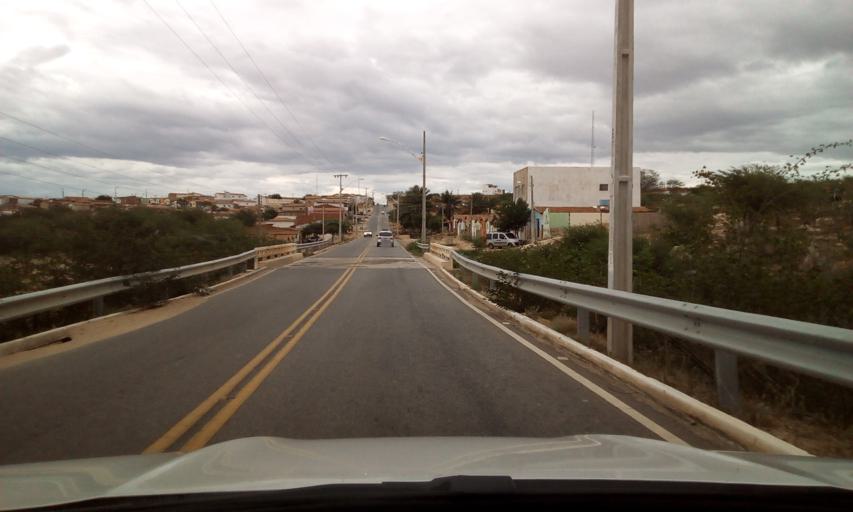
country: BR
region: Paraiba
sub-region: Picui
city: Picui
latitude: -6.5135
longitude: -36.3364
